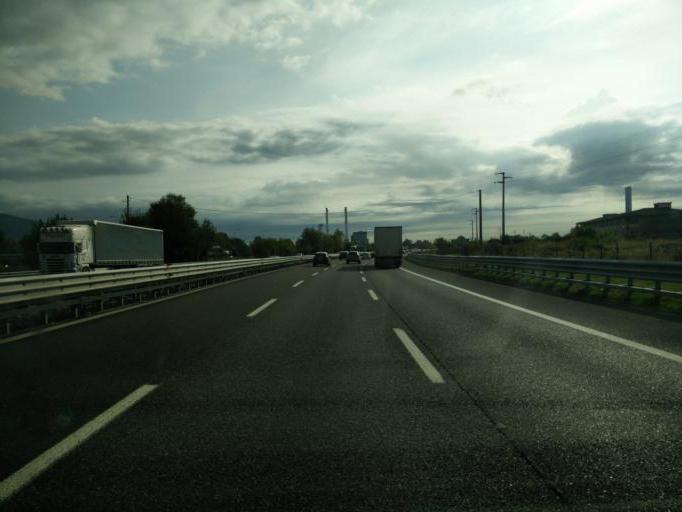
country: IT
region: Lombardy
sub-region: Provincia di Brescia
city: Brescia
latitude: 45.5187
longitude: 10.1972
